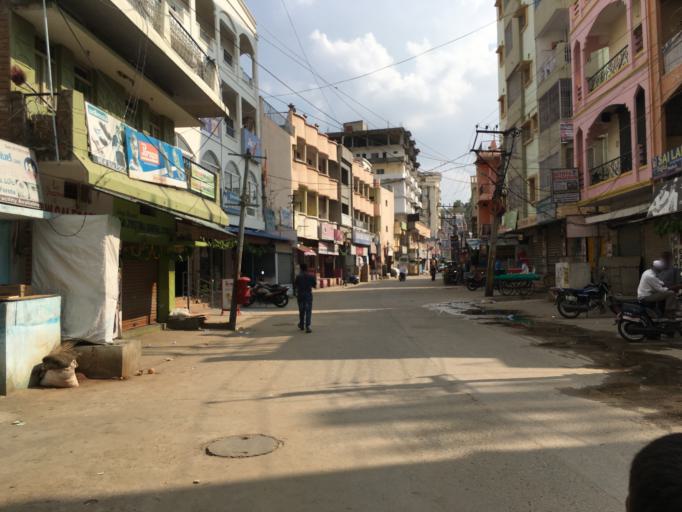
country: IN
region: Andhra Pradesh
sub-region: Anantapur
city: Puttaparthi
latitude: 14.1681
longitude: 77.8112
